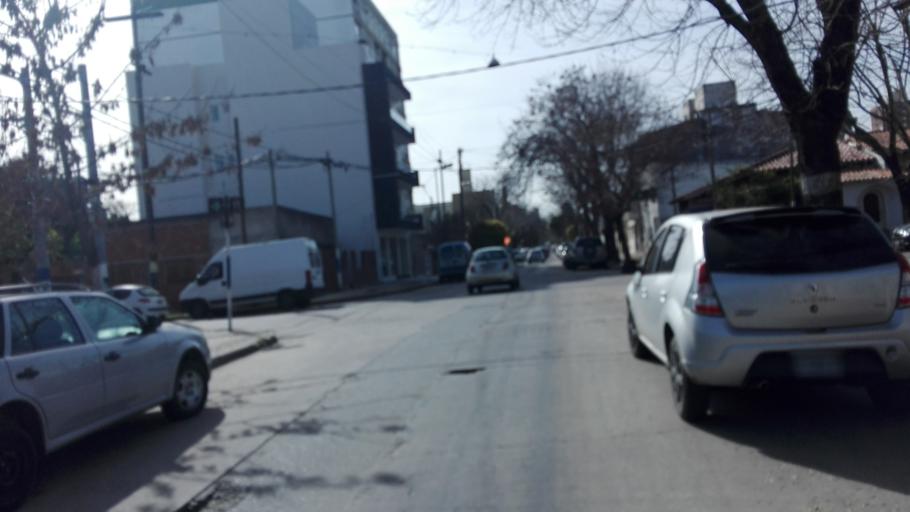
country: AR
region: Buenos Aires
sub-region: Partido de La Plata
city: La Plata
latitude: -34.9079
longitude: -57.9688
